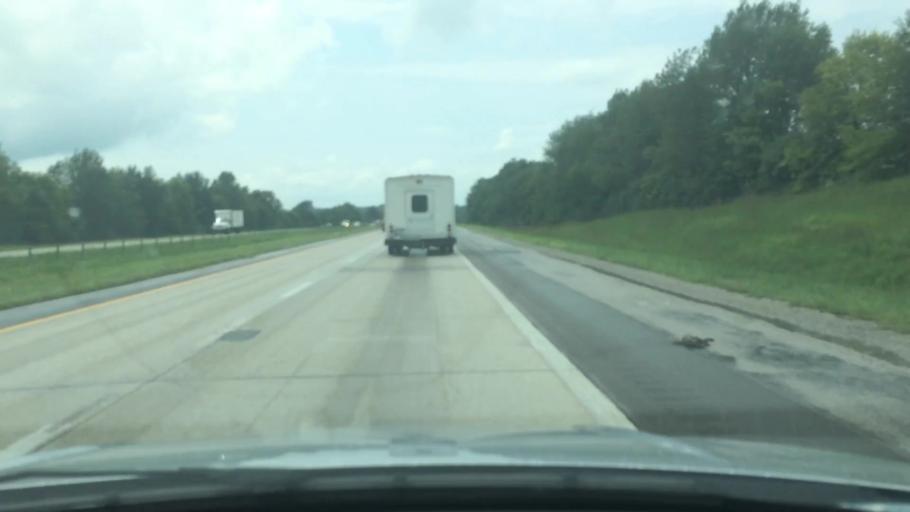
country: US
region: Kentucky
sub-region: Woodford County
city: Midway
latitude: 38.1627
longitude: -84.7286
